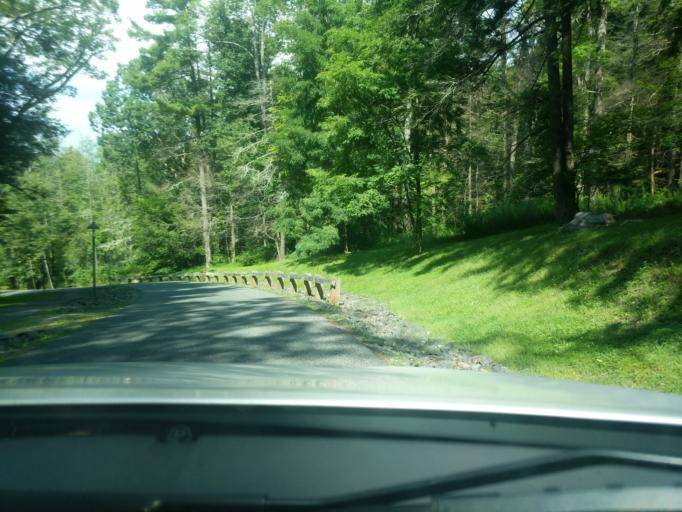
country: US
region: Massachusetts
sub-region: Berkshire County
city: Great Barrington
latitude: 42.2088
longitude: -73.3739
